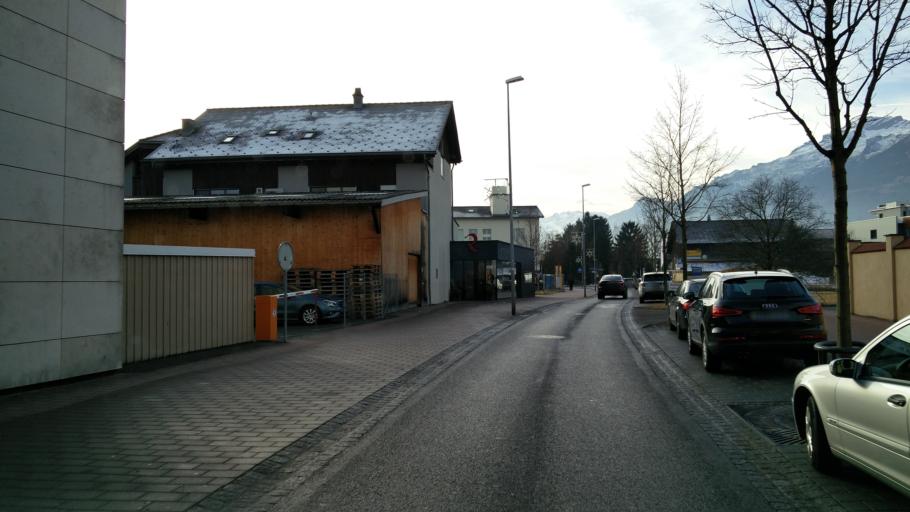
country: LI
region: Schaan
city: Schaan
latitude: 47.1666
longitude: 9.5087
